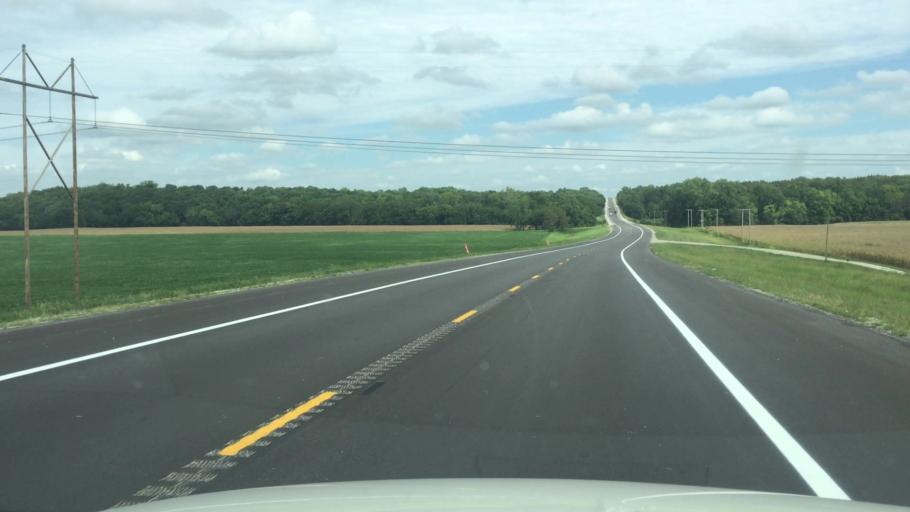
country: US
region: Kansas
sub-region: Anderson County
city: Garnett
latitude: 38.3351
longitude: -95.2489
